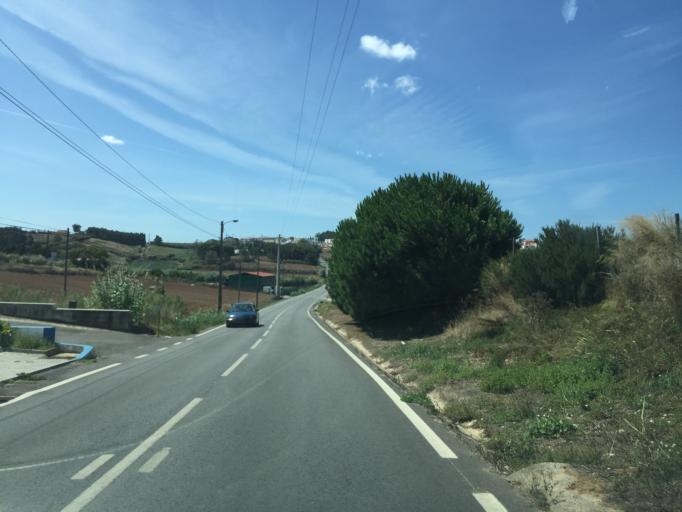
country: PT
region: Lisbon
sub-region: Lourinha
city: Lourinha
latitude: 39.2638
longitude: -9.3131
